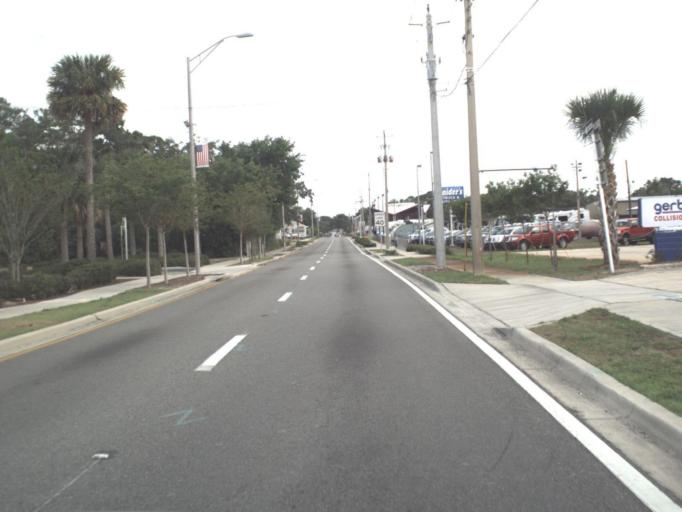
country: US
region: Florida
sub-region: Brevard County
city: Titusville
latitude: 28.6067
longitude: -80.8085
